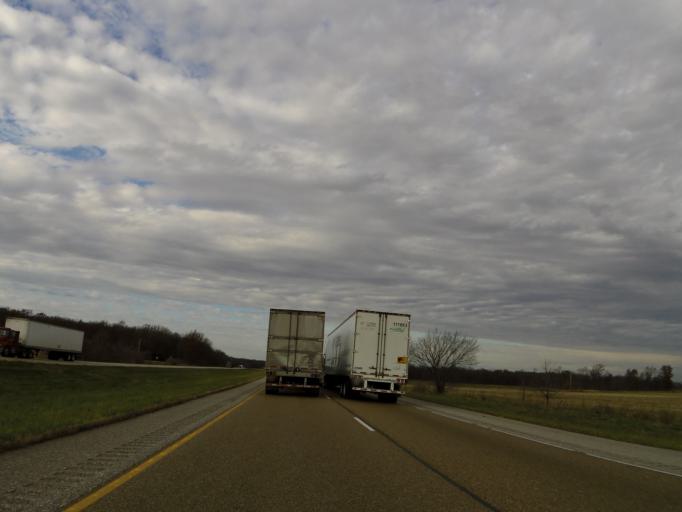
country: US
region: Illinois
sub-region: Washington County
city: Nashville
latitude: 38.3913
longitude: -89.2910
